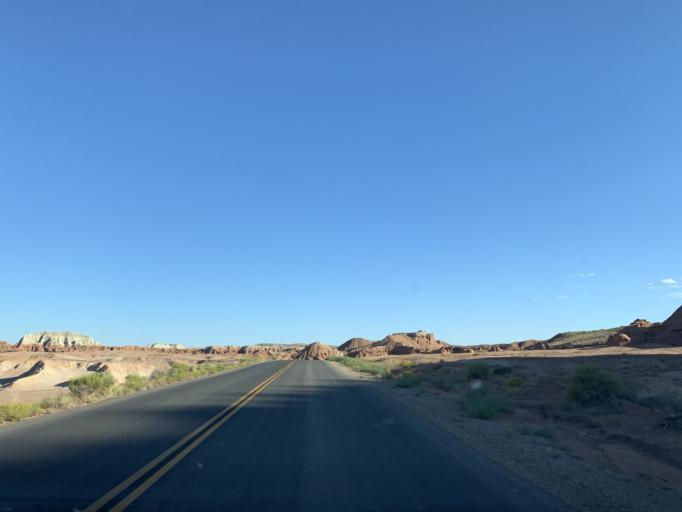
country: US
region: Utah
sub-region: Emery County
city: Ferron
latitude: 38.5702
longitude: -110.7081
